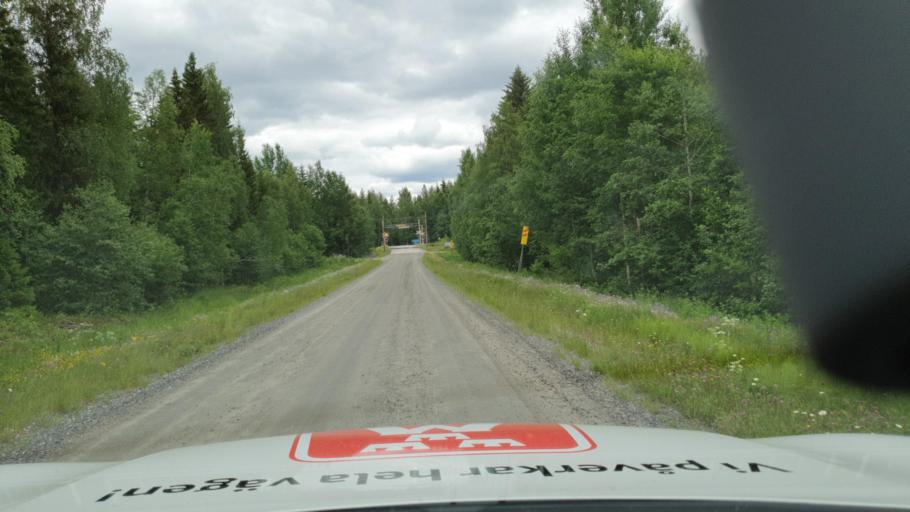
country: SE
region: Vaesterbotten
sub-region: Bjurholms Kommun
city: Bjurholm
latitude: 63.7672
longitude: 19.2636
